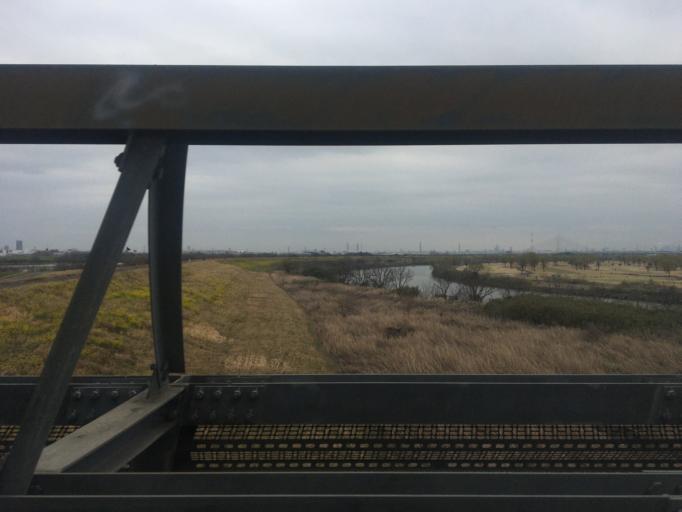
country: JP
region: Saitama
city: Asaka
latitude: 35.8323
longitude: 139.6142
